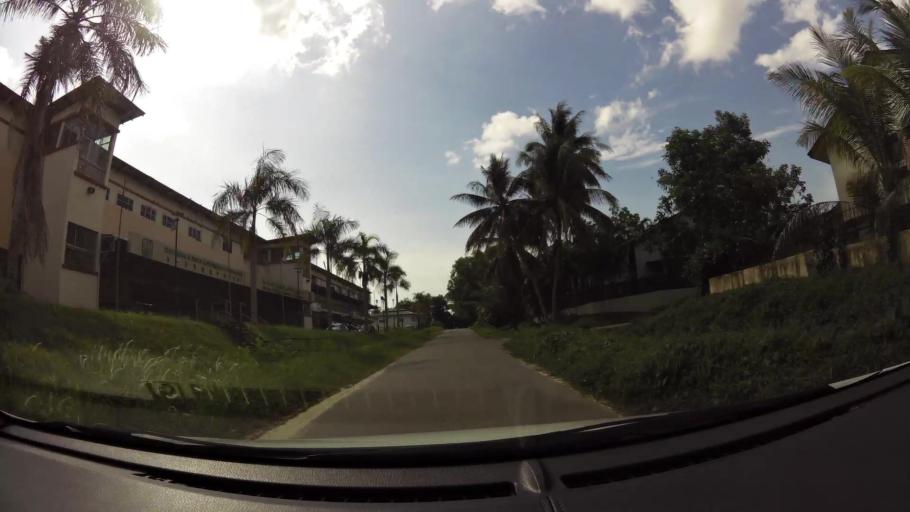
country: BN
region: Brunei and Muara
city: Bandar Seri Begawan
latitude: 4.9498
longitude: 114.9680
